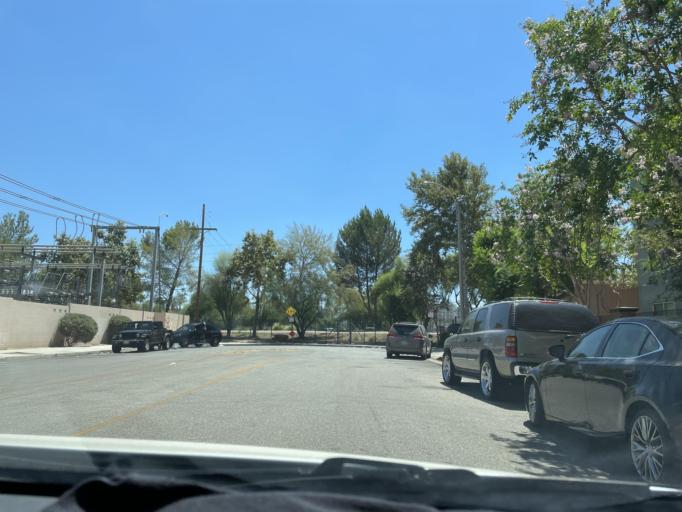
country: US
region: California
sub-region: Los Angeles County
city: Canoga Park
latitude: 34.1895
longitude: -118.5928
